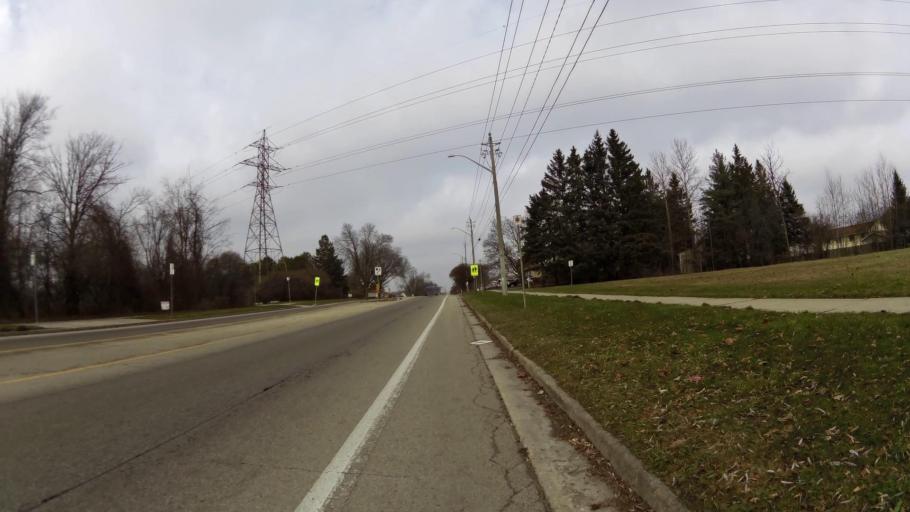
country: CA
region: Ontario
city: Kitchener
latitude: 43.4187
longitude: -80.4830
